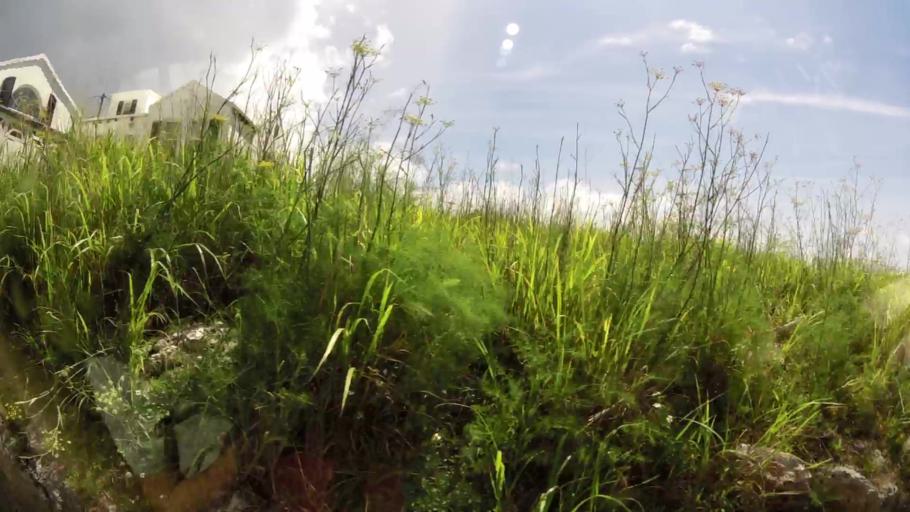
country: BM
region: Saint George
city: Saint George
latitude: 32.3657
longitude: -64.6530
